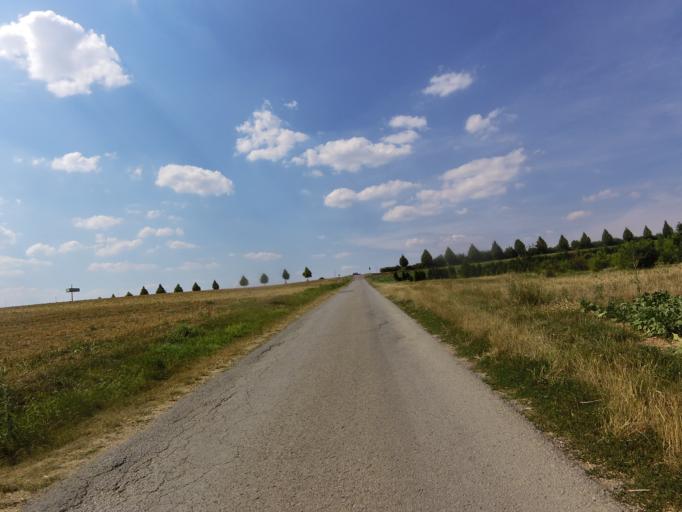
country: DE
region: Bavaria
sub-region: Regierungsbezirk Unterfranken
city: Estenfeld
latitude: 49.8183
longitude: 9.9920
